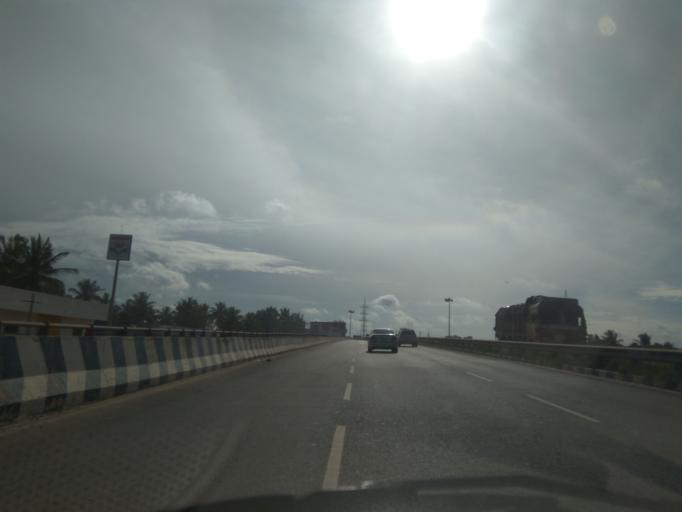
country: IN
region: Karnataka
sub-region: Bangalore Rural
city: Hoskote
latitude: 13.0774
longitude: 77.7994
